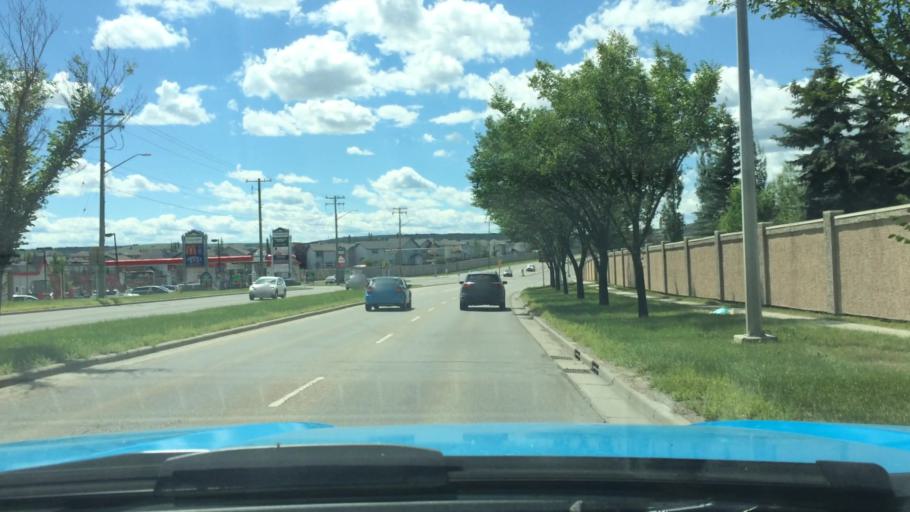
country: CA
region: Alberta
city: Calgary
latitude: 51.1497
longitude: -114.0716
